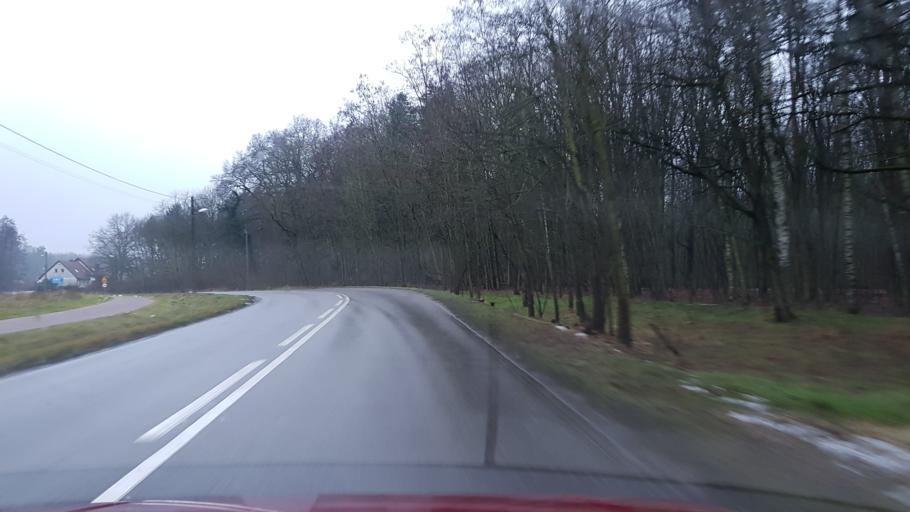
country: PL
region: West Pomeranian Voivodeship
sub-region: Powiat policki
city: Police
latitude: 53.5301
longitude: 14.5365
